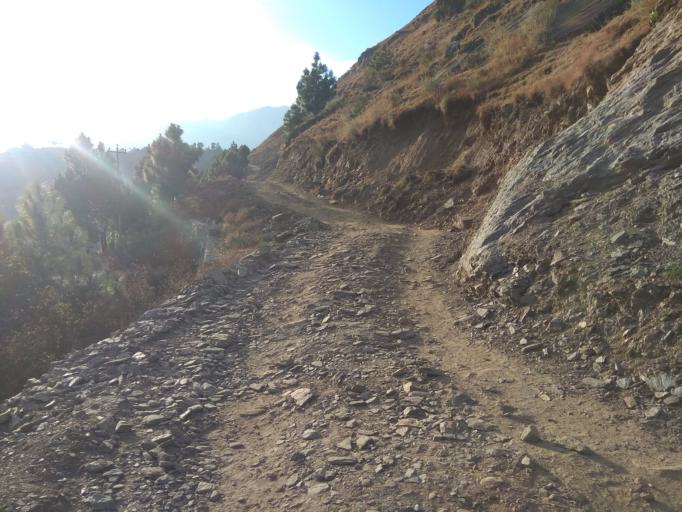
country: NP
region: Far Western
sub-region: Seti Zone
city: Achham
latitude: 29.2487
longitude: 81.6542
